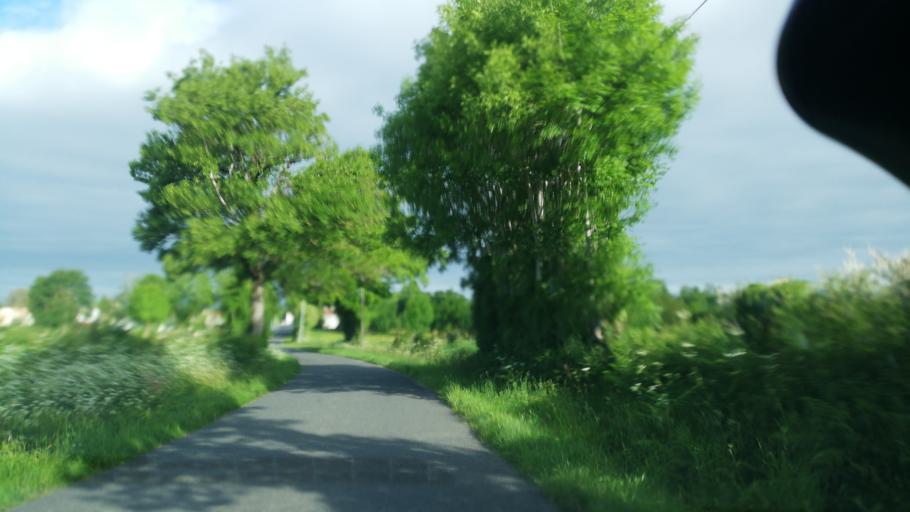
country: FR
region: Poitou-Charentes
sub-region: Departement des Deux-Sevres
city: Moncoutant
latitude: 46.6830
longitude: -0.5701
